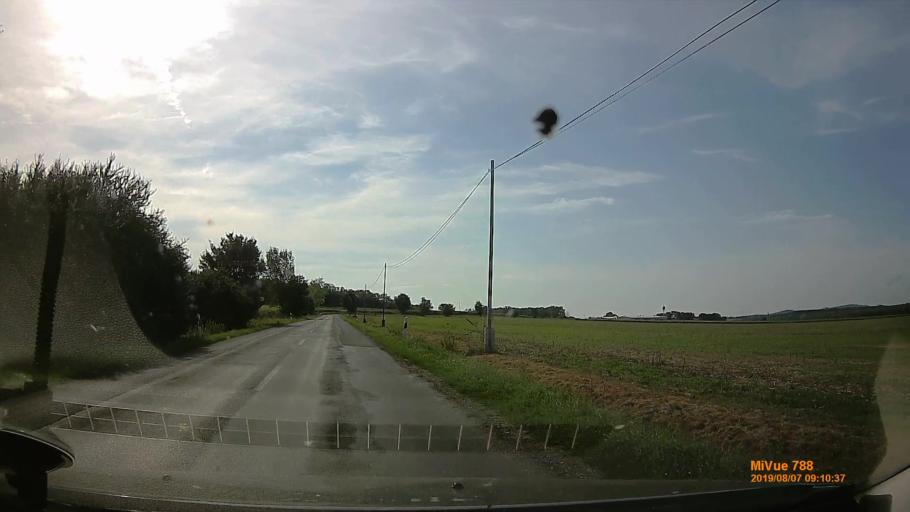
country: HU
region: Zala
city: Pacsa
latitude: 46.7298
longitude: 17.0849
